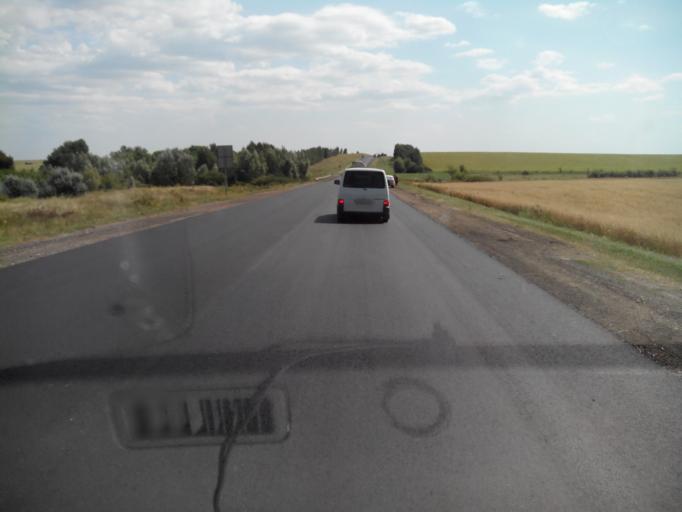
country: RU
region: Saratov
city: Svetlyy
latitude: 51.7225
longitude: 45.7588
